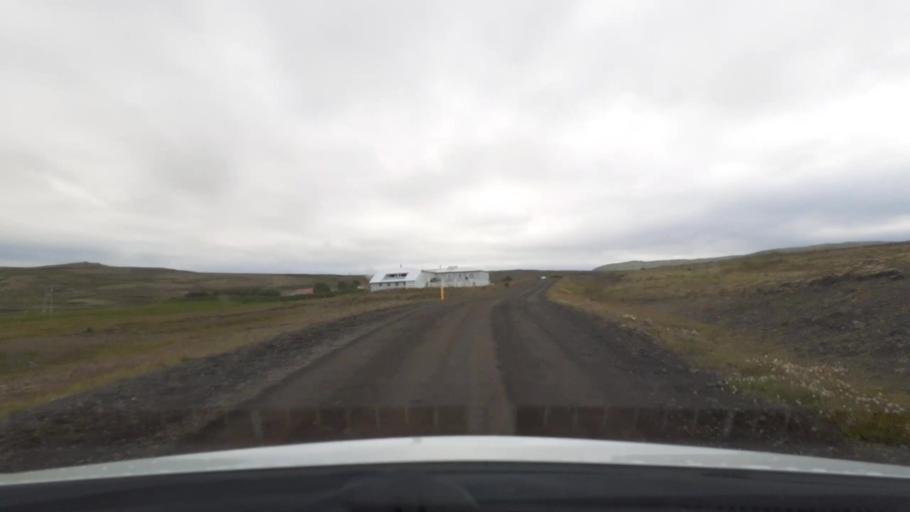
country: IS
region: Capital Region
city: Mosfellsbaer
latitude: 64.2059
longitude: -21.5635
